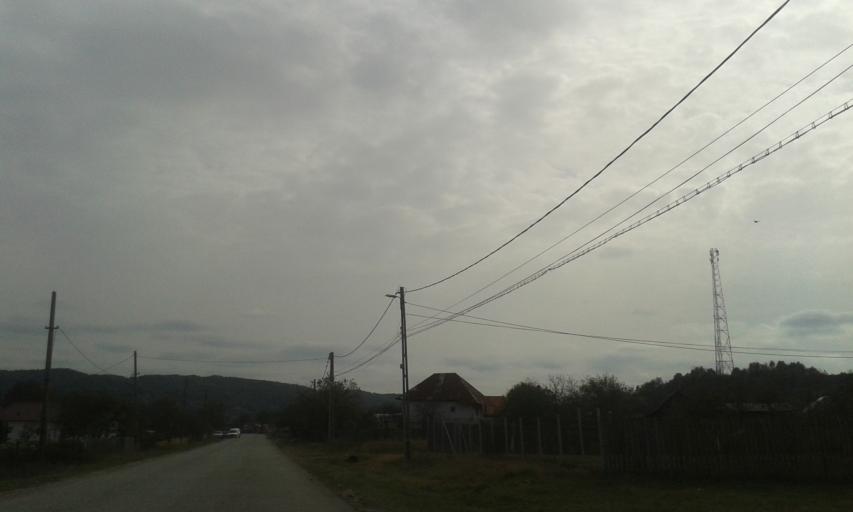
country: RO
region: Gorj
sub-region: Comuna Hurezani
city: Hurezani
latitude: 44.8196
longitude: 23.6510
